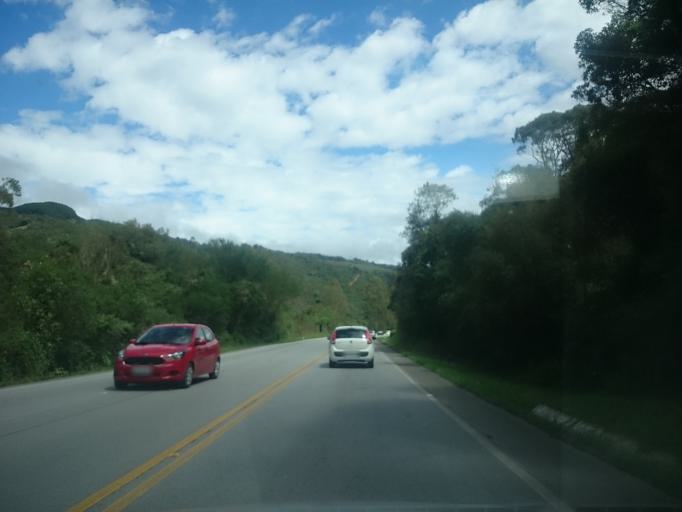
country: BR
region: Santa Catarina
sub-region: Anitapolis
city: Anitapolis
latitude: -27.6684
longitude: -49.2048
